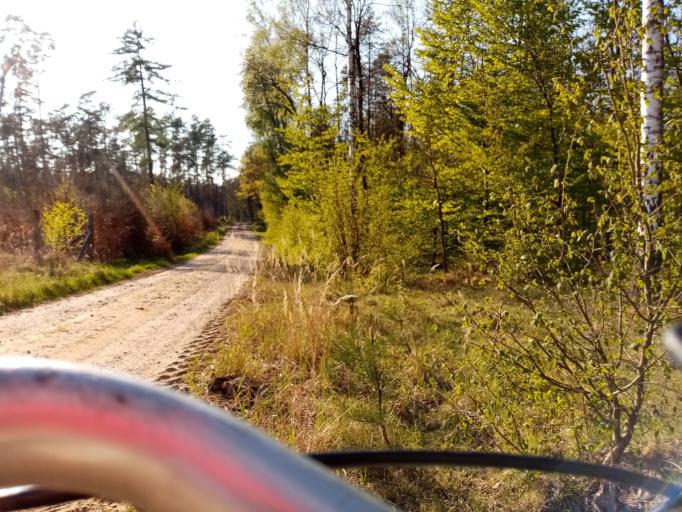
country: PL
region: Kujawsko-Pomorskie
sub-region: Powiat brodnicki
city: Gorzno
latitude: 53.1698
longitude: 19.6698
